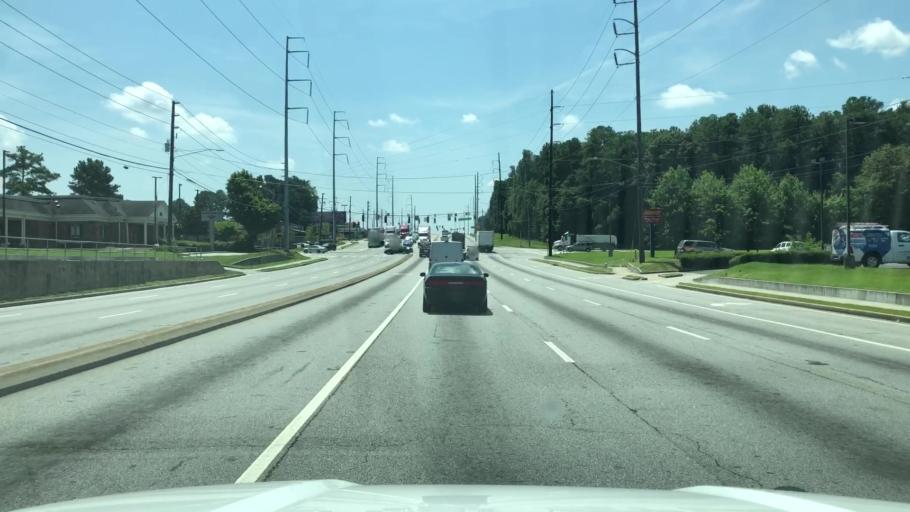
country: US
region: Georgia
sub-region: Gwinnett County
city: Norcross
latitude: 33.9191
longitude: -84.2102
